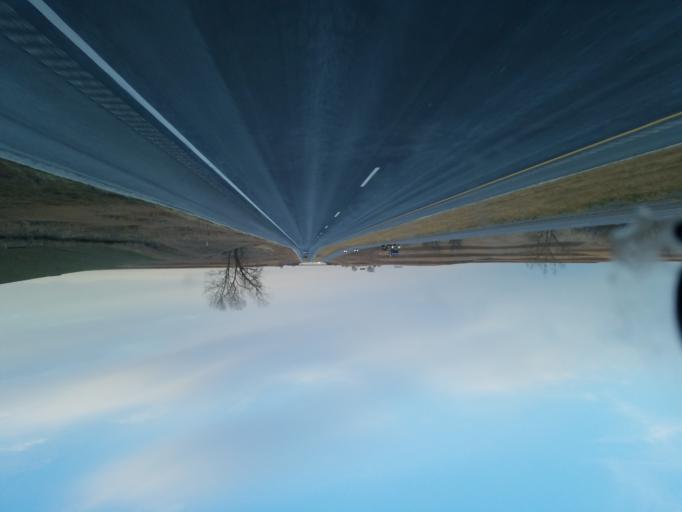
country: US
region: Iowa
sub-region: Harrison County
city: Logan
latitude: 41.4991
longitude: -95.7211
